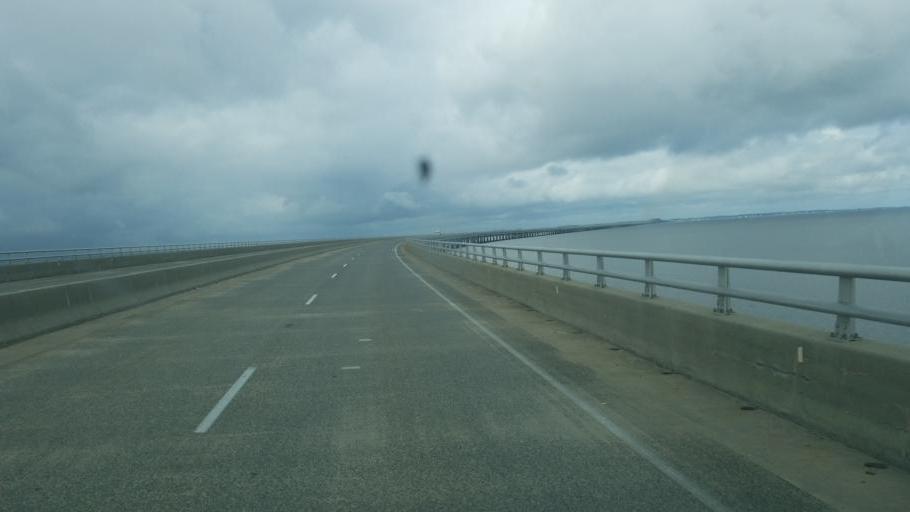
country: US
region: North Carolina
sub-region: Dare County
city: Manteo
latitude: 35.8831
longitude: -75.6762
